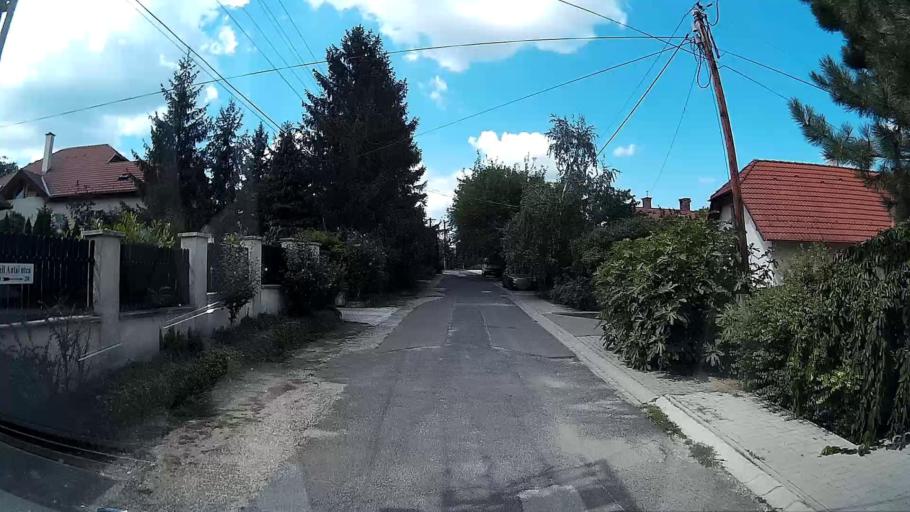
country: HU
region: Pest
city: Szentendre
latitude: 47.6724
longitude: 19.0608
